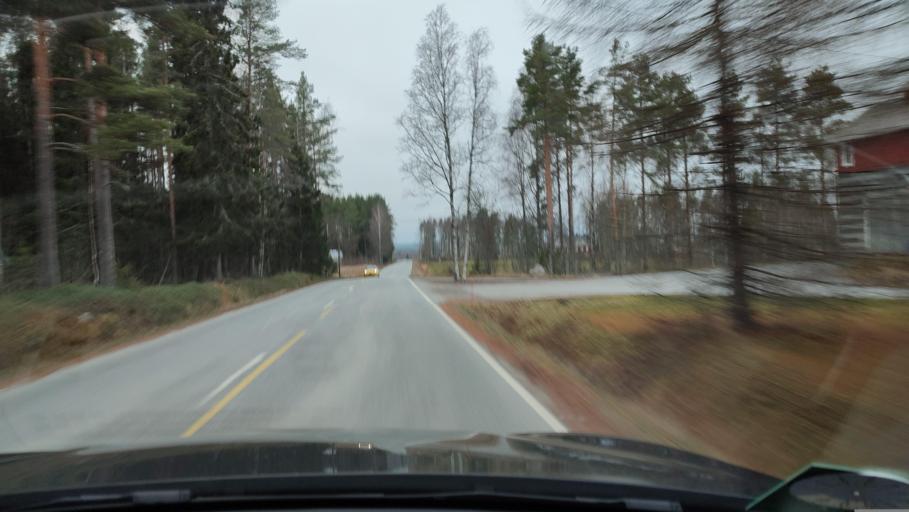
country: FI
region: Southern Ostrobothnia
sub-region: Suupohja
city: Karijoki
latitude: 62.2641
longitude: 21.7297
